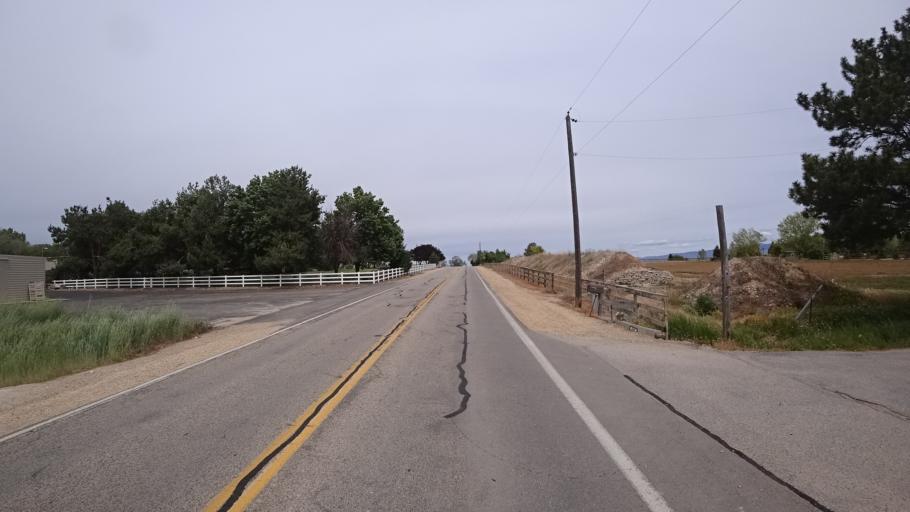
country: US
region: Idaho
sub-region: Ada County
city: Meridian
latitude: 43.5539
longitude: -116.3746
